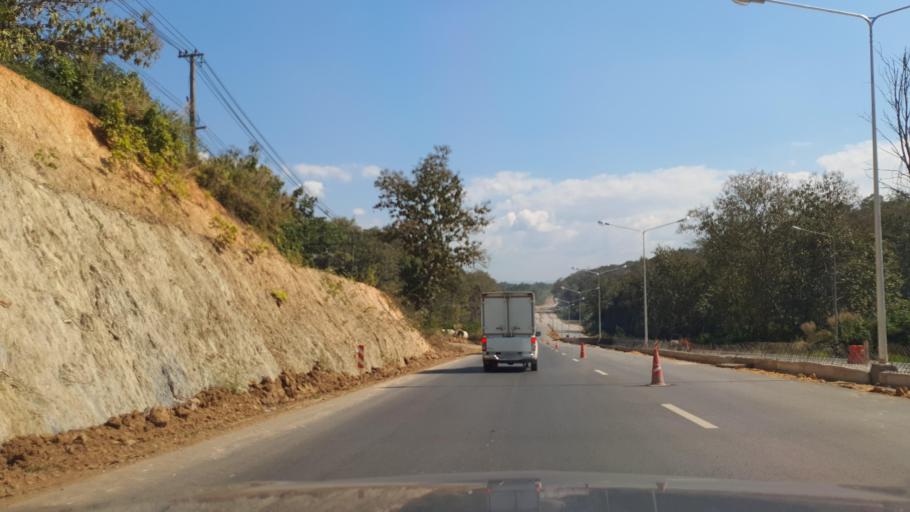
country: TH
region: Nan
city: Nan
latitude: 18.8304
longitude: 100.7529
